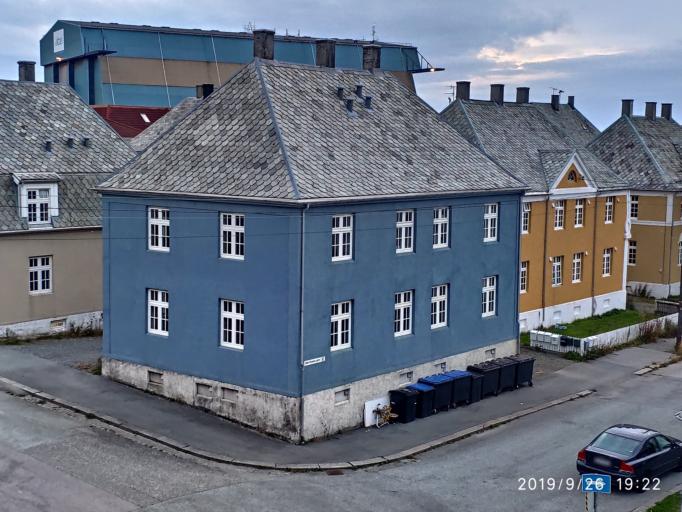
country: NO
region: Rogaland
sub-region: Haugesund
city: Haugesund
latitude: 59.4100
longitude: 5.2671
